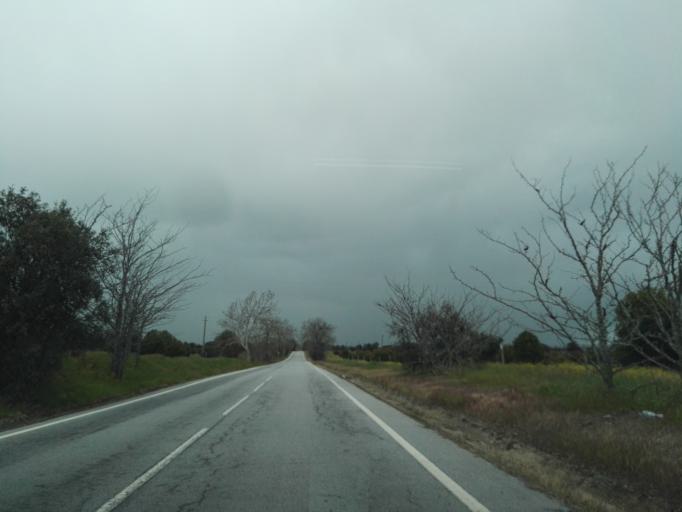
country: PT
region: Portalegre
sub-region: Arronches
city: Arronches
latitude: 39.0167
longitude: -7.2565
